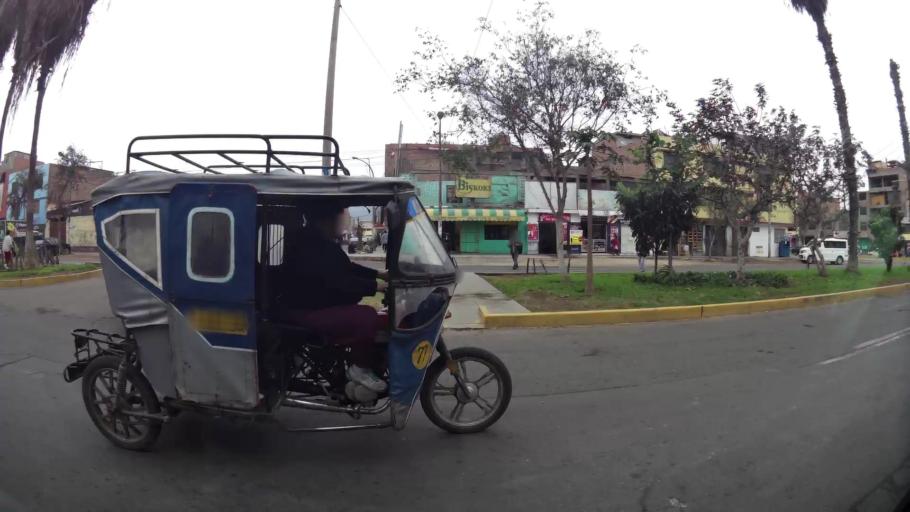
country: PE
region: Lima
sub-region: Lima
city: Independencia
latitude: -11.9717
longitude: -77.0726
